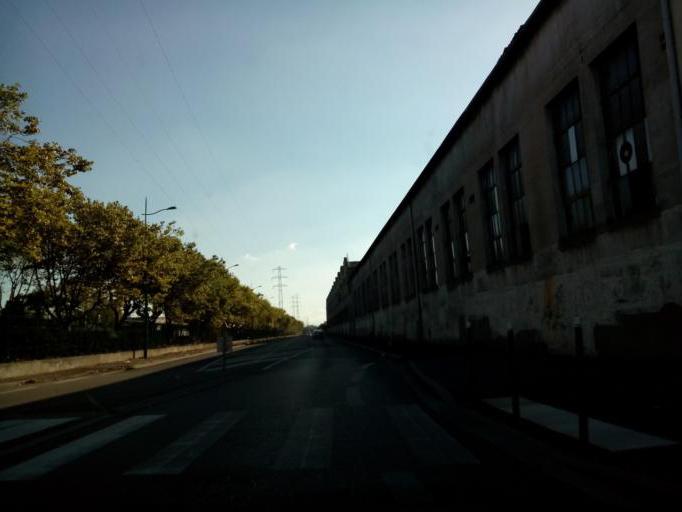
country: FR
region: Rhone-Alpes
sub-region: Departement du Rhone
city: Bron
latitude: 45.7092
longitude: 4.9001
